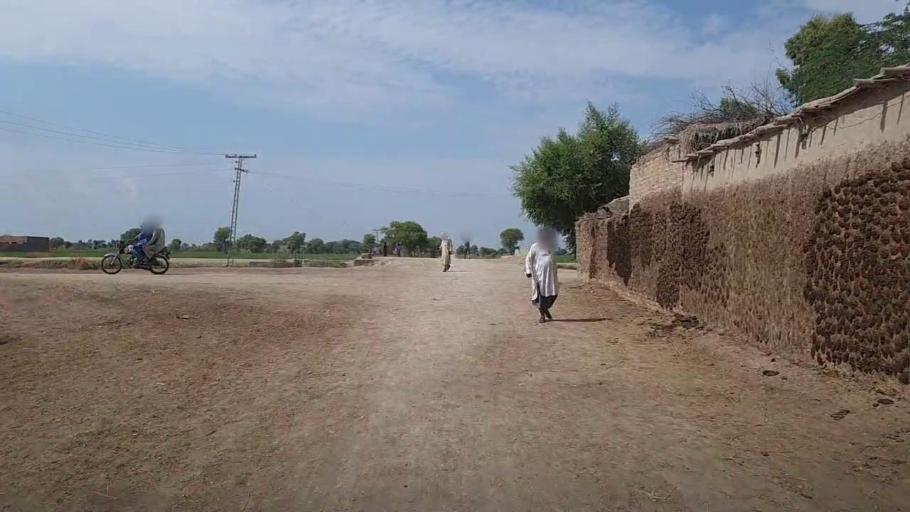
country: PK
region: Sindh
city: Thul
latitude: 28.2477
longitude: 68.8090
